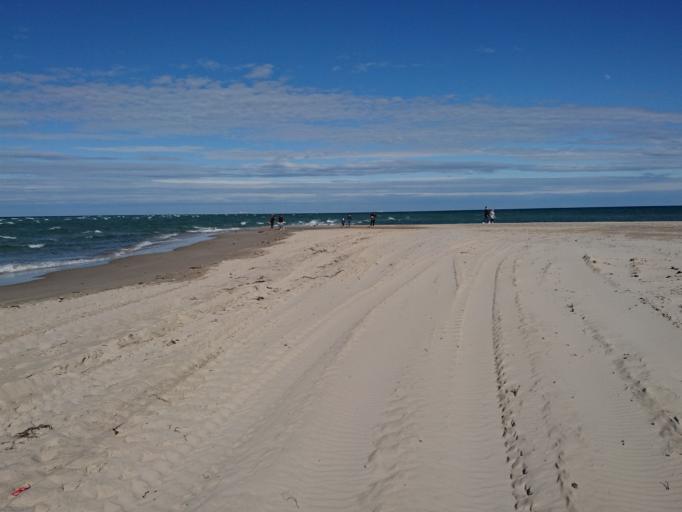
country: DK
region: North Denmark
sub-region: Frederikshavn Kommune
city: Skagen
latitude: 57.7468
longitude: 10.6508
